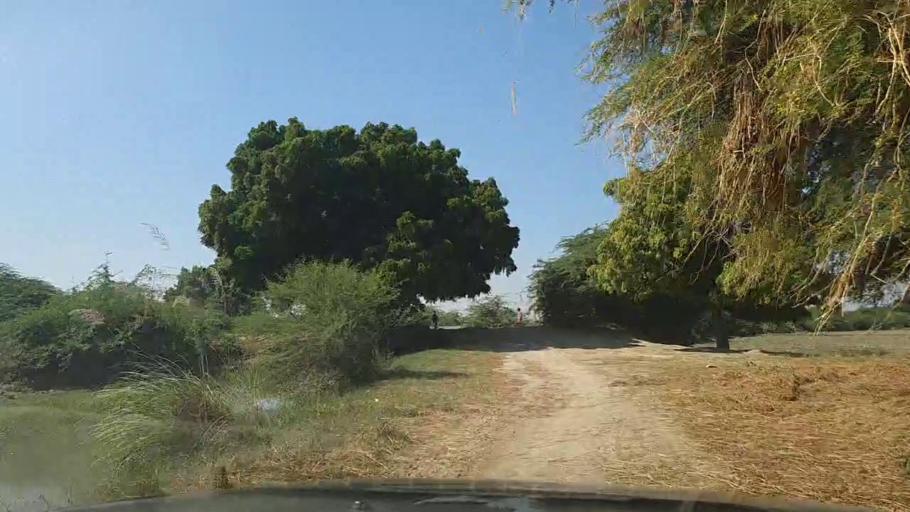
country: PK
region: Sindh
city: Mirpur Sakro
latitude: 24.5748
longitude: 67.7889
